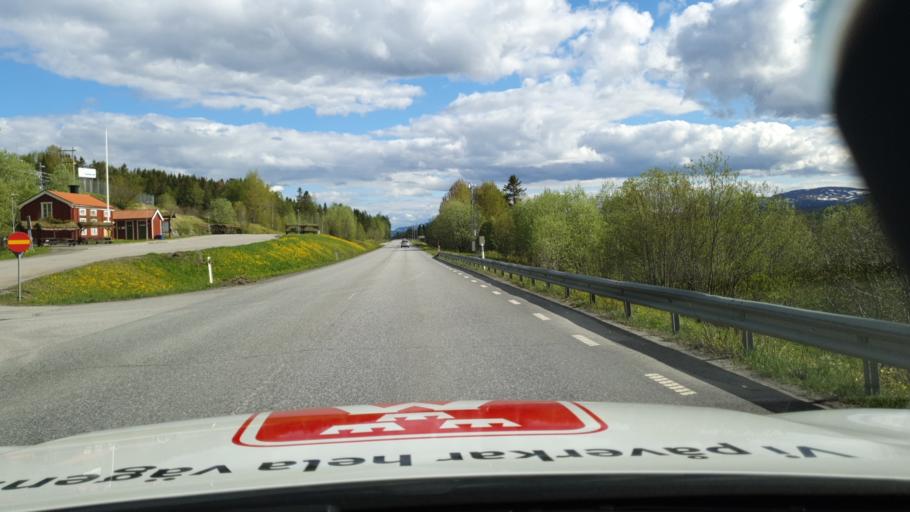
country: SE
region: Jaemtland
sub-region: Are Kommun
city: Are
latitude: 63.3744
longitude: 13.1601
